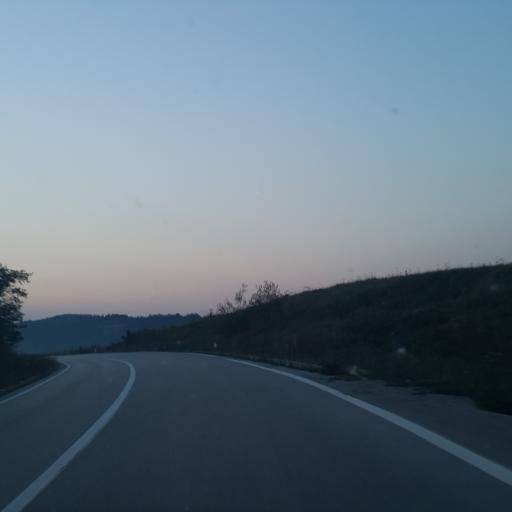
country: RS
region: Central Serbia
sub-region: Nisavski Okrug
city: Svrljig
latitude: 43.4532
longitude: 22.1888
